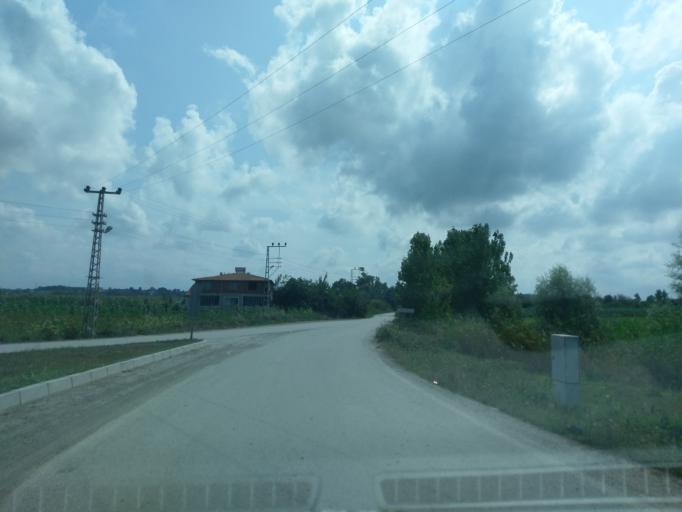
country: TR
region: Samsun
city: Bafra
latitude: 41.6027
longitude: 35.8032
